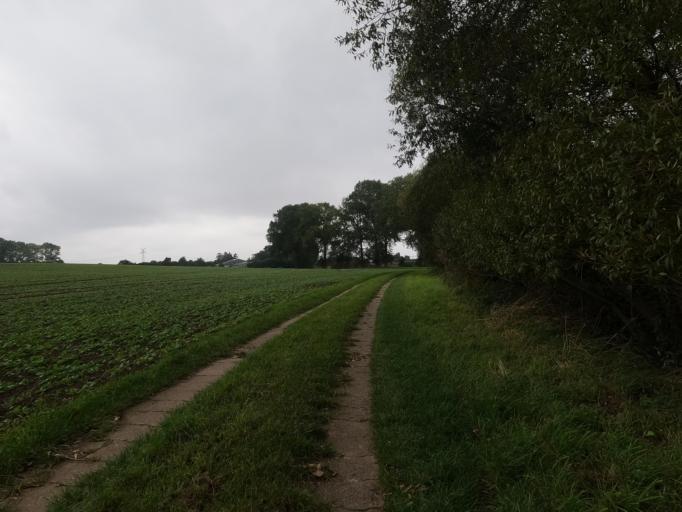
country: DE
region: Schleswig-Holstein
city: Heiligenhafen
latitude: 54.3593
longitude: 10.9940
